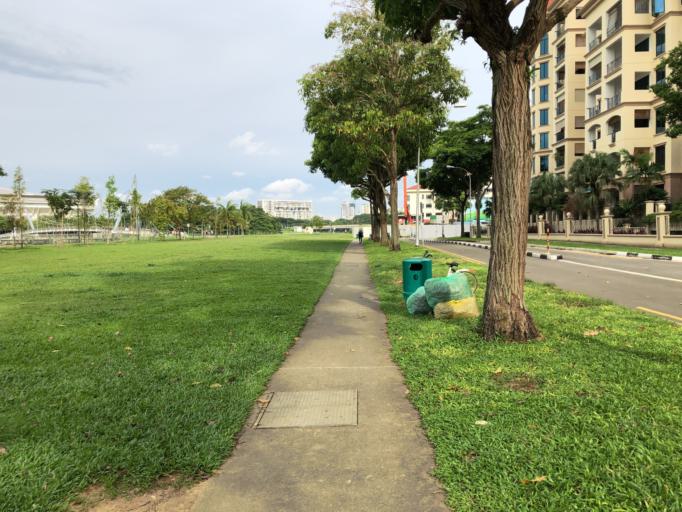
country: SG
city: Singapore
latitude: 1.2981
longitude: 103.8723
